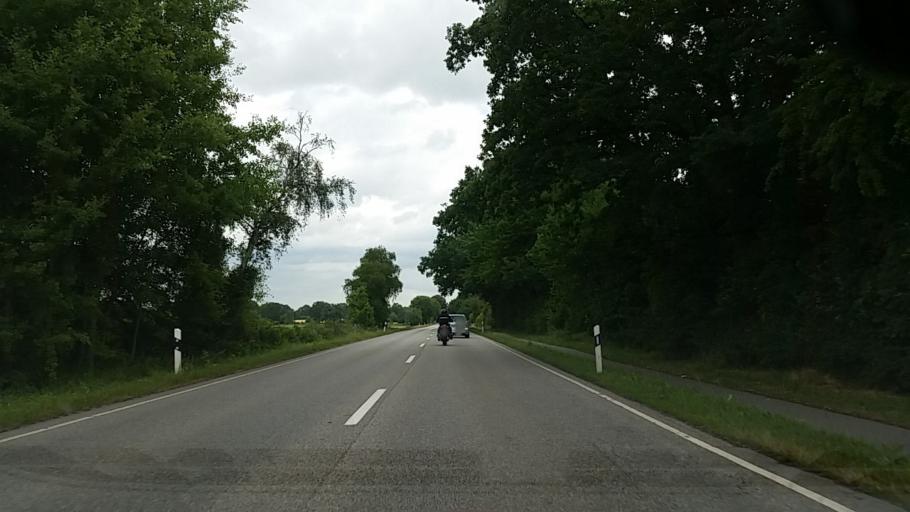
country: DE
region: Schleswig-Holstein
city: Tangstedt
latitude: 53.7159
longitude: 10.0803
